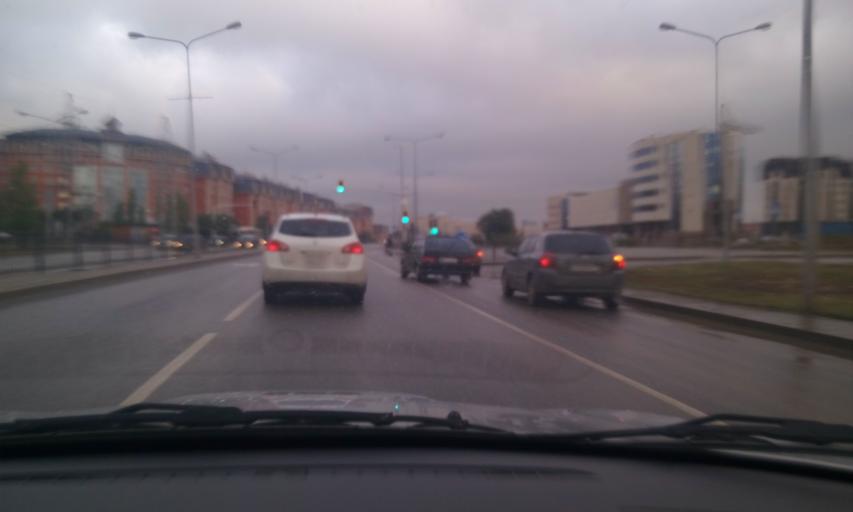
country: KZ
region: Astana Qalasy
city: Astana
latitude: 51.1477
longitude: 71.3811
